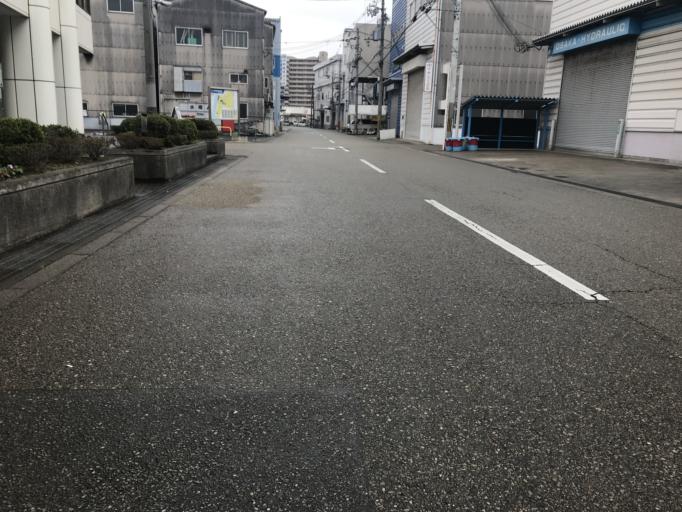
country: JP
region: Osaka
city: Sakai
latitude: 34.6255
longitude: 135.4712
